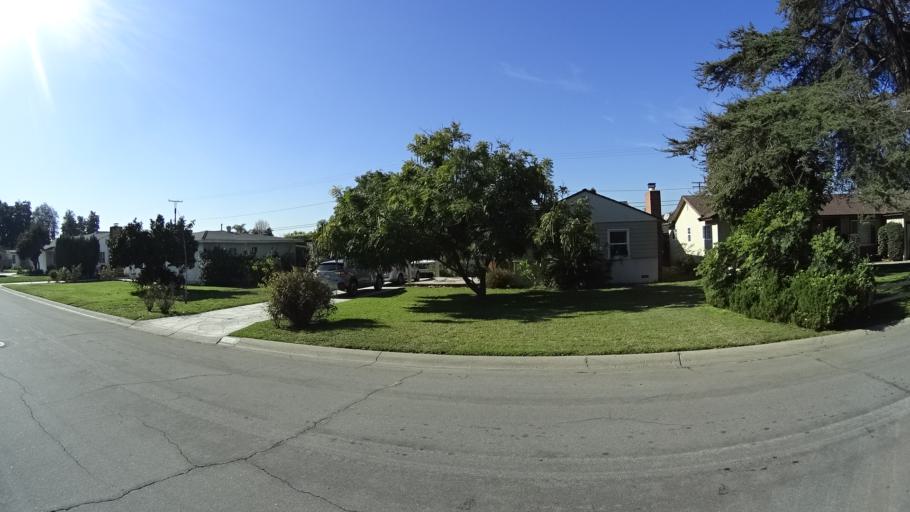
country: US
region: California
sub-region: Orange County
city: Garden Grove
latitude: 33.7831
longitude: -117.9351
